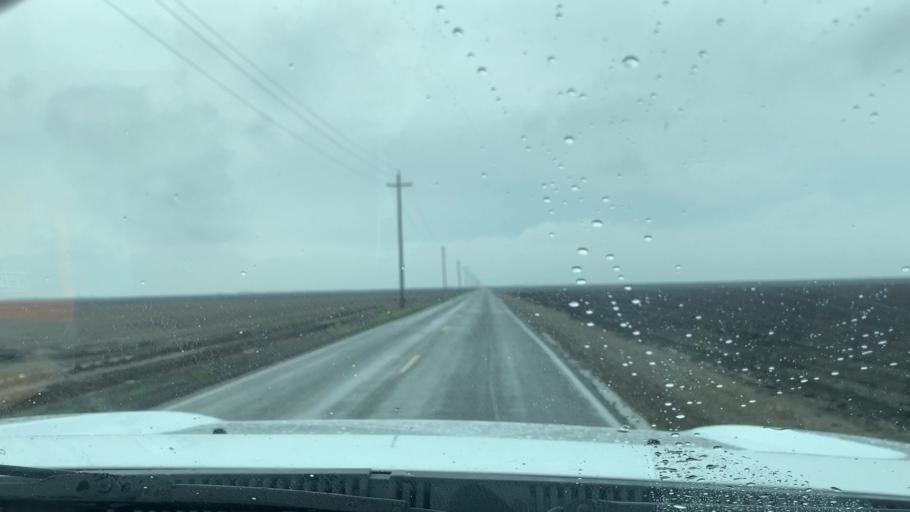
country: US
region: California
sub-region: Tulare County
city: Alpaugh
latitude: 35.9738
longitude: -119.5720
